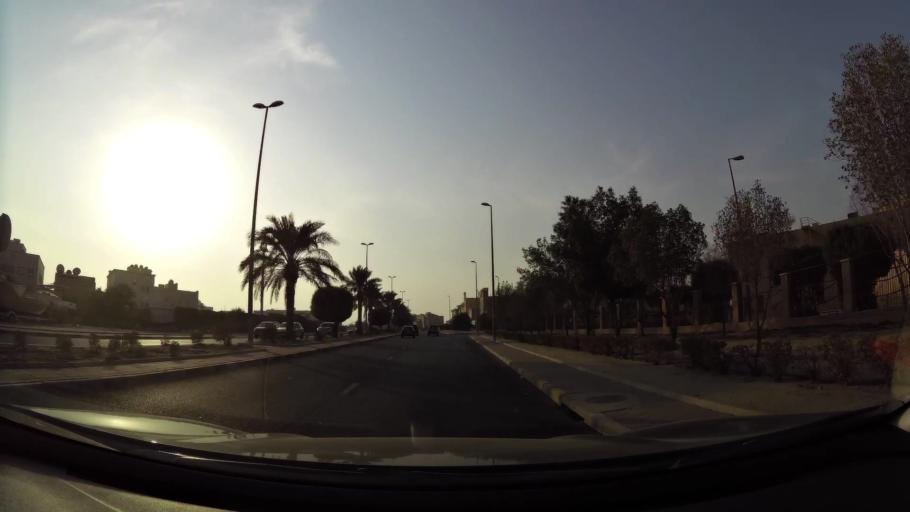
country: KW
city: Al Funaytis
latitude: 29.2217
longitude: 48.0685
